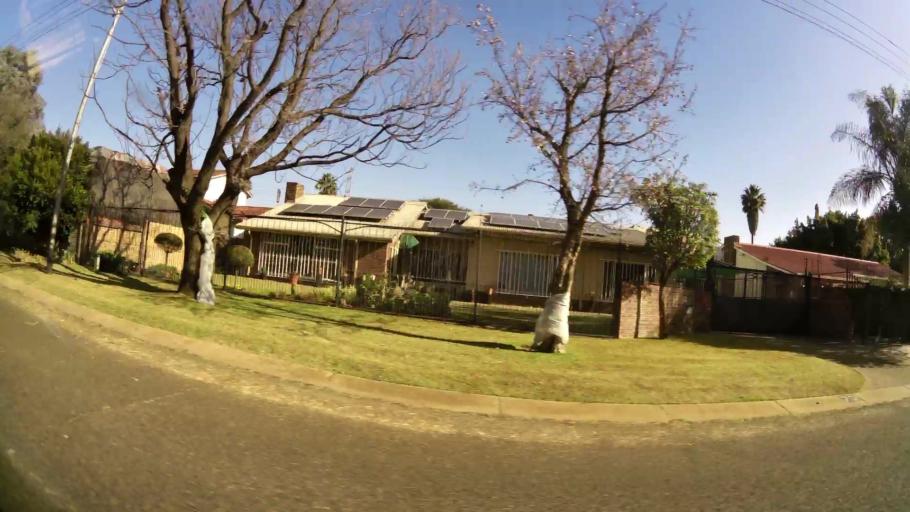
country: ZA
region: Gauteng
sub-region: City of Tshwane Metropolitan Municipality
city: Pretoria
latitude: -25.7236
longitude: 28.2626
